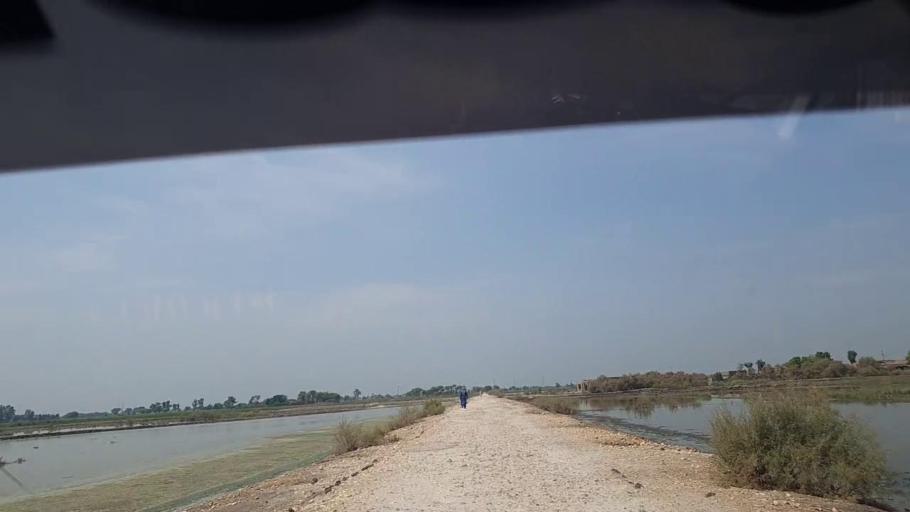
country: PK
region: Sindh
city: Thul
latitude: 28.1700
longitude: 68.7567
